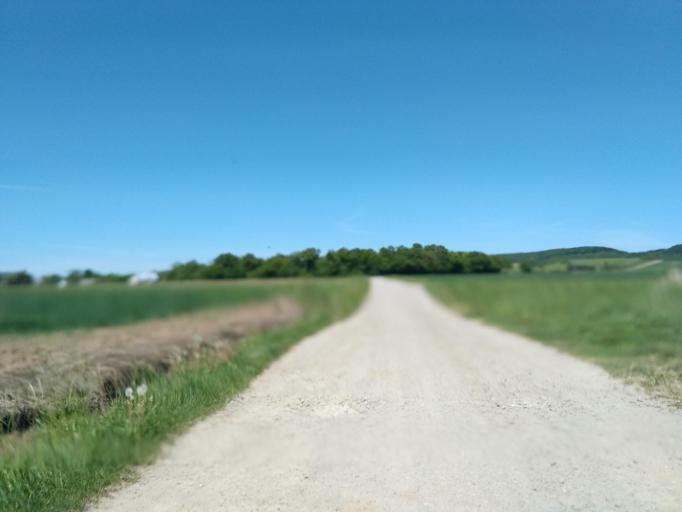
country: PL
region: Subcarpathian Voivodeship
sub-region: Powiat sanocki
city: Dlugie
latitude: 49.6029
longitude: 22.0371
